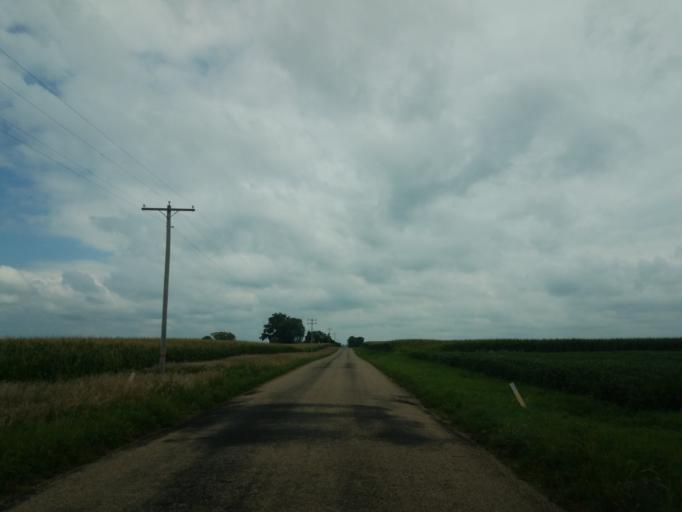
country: US
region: Illinois
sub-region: McLean County
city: Twin Grove
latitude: 40.4190
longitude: -89.0621
